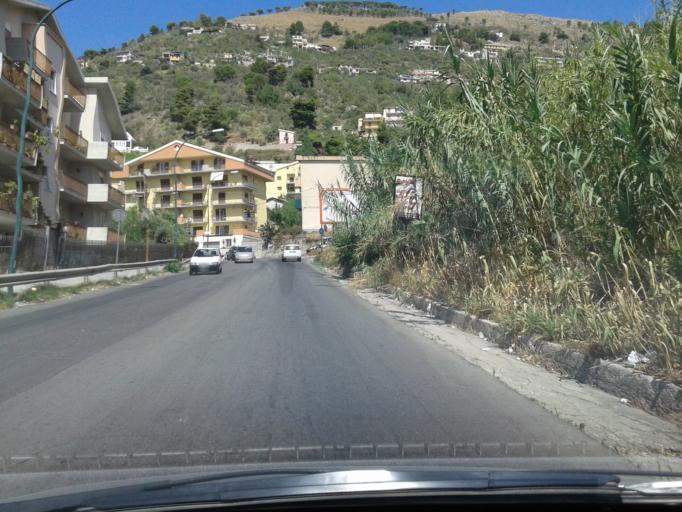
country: IT
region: Sicily
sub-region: Palermo
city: Monreale
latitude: 38.0755
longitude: 13.2822
